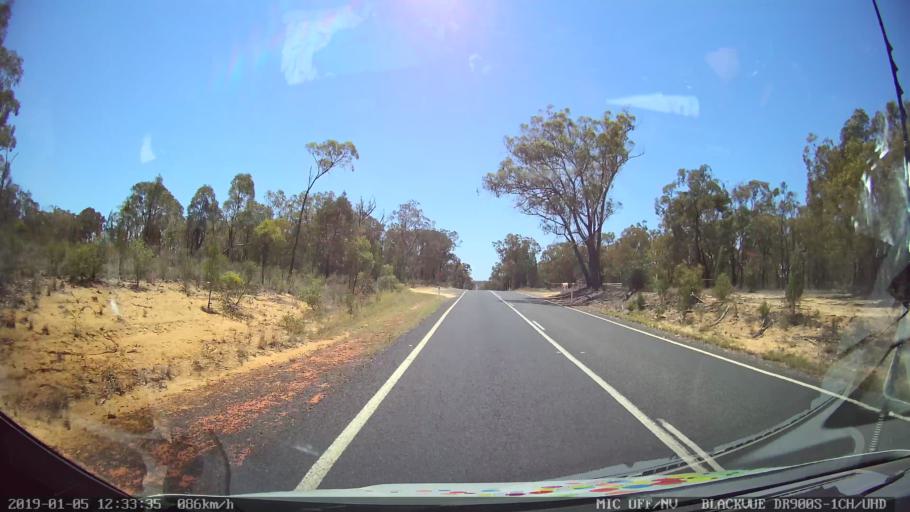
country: AU
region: New South Wales
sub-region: Warrumbungle Shire
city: Coonabarabran
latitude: -31.2143
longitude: 149.3973
